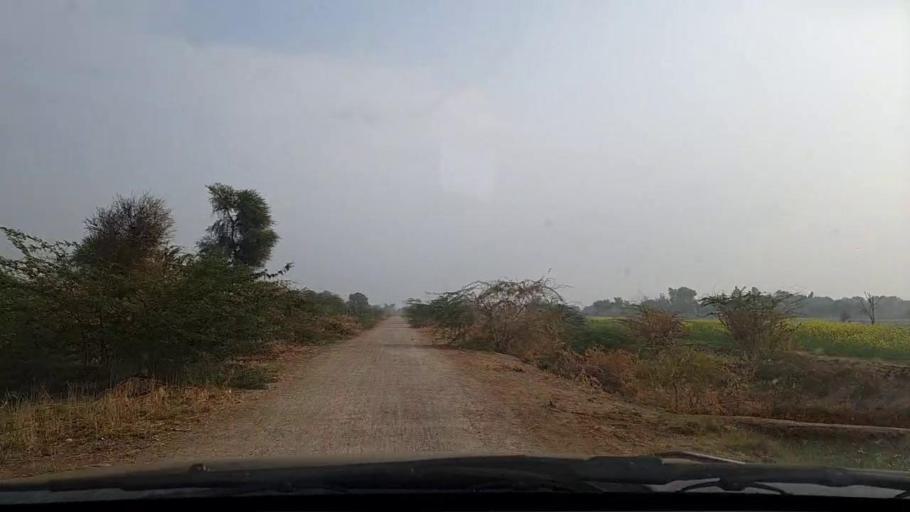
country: PK
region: Sindh
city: Pithoro
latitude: 25.7045
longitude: 69.3874
